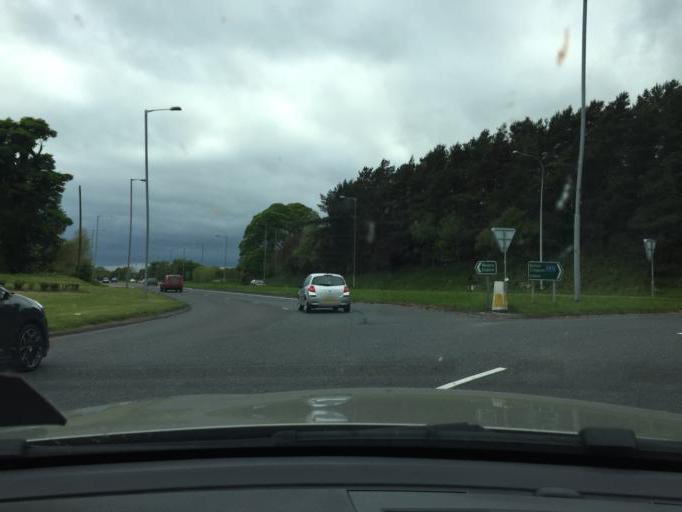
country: GB
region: Northern Ireland
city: Hillsborough
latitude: 54.4727
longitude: -6.0776
